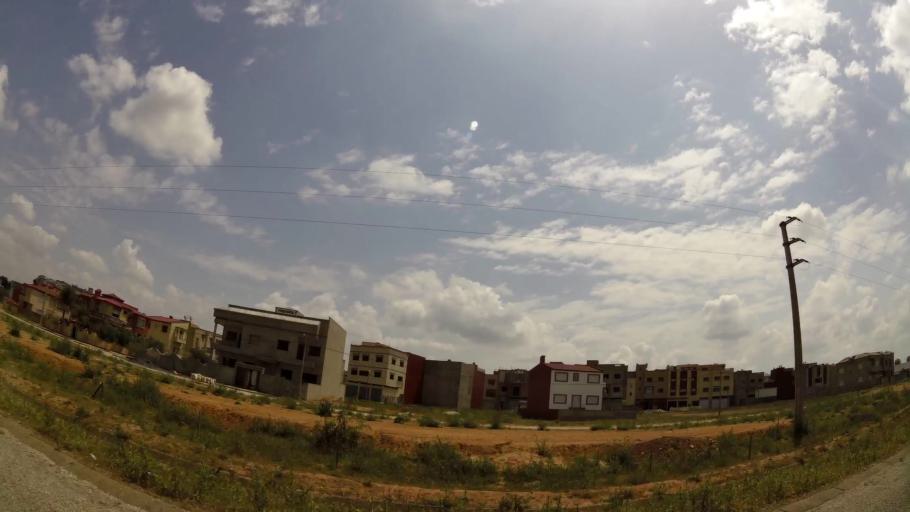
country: MA
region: Gharb-Chrarda-Beni Hssen
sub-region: Kenitra Province
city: Kenitra
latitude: 34.0100
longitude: -6.5403
